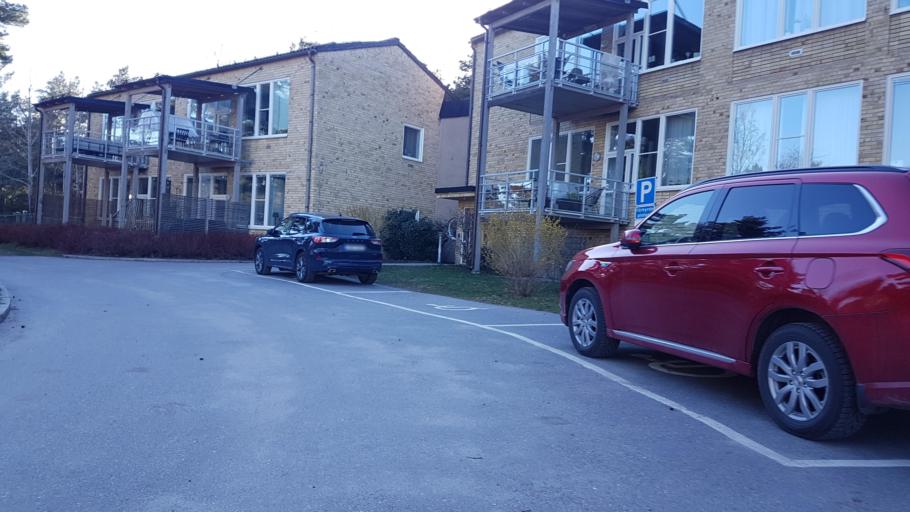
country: SE
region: Stockholm
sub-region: Stockholms Kommun
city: Arsta
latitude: 59.2658
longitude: 18.0742
